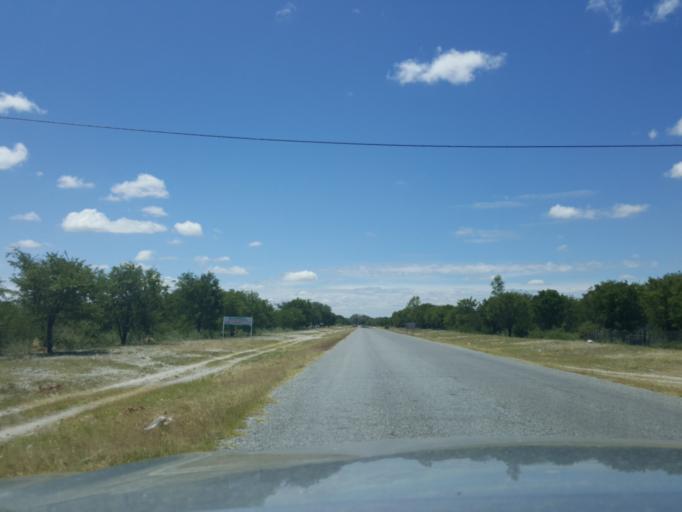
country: BW
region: Central
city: Nata
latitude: -20.2134
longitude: 26.1699
